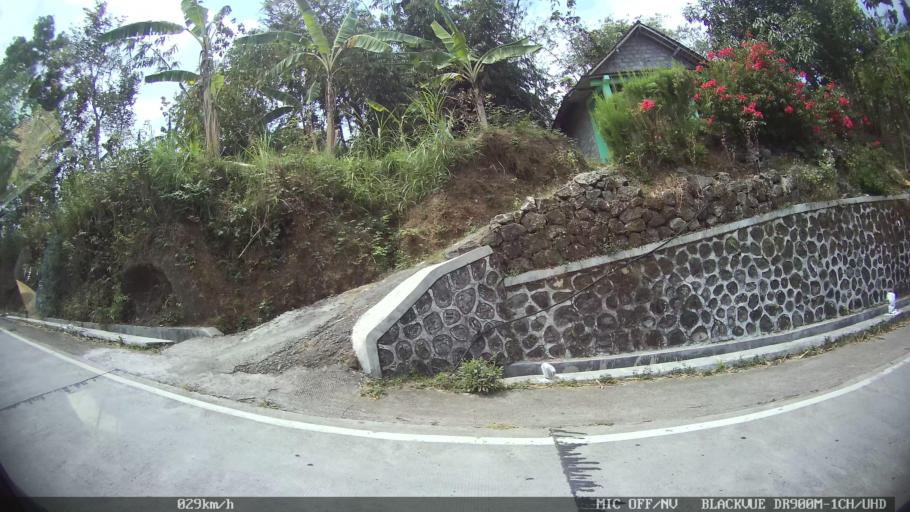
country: ID
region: Central Java
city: Candi Prambanan
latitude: -7.7916
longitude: 110.5183
